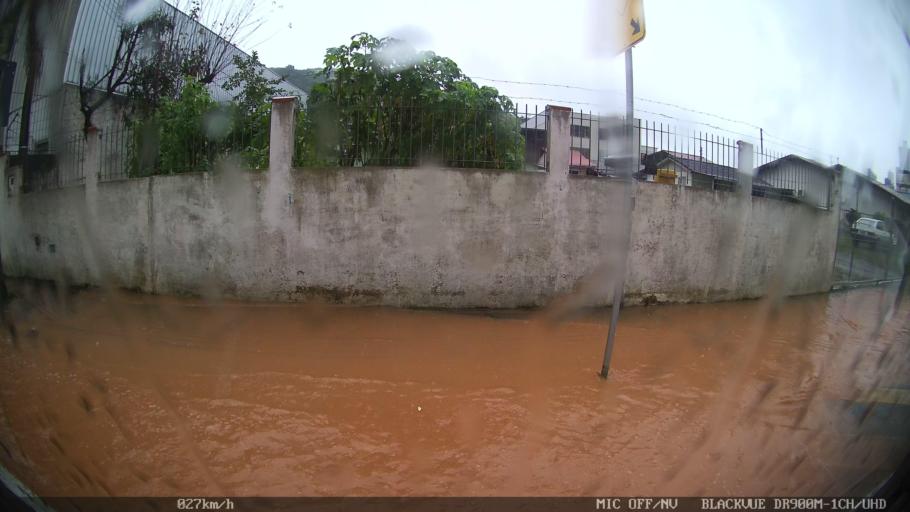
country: BR
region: Santa Catarina
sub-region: Balneario Camboriu
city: Balneario Camboriu
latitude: -26.9902
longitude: -48.6417
